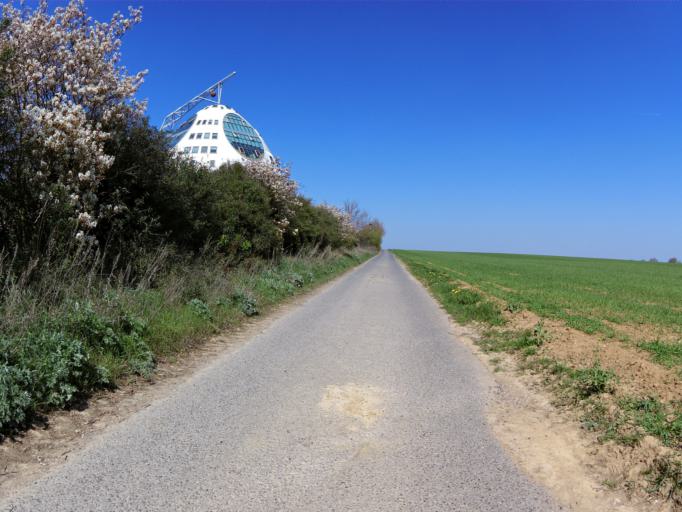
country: DE
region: Bavaria
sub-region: Regierungsbezirk Unterfranken
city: Biebelried
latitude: 49.7783
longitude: 10.0711
